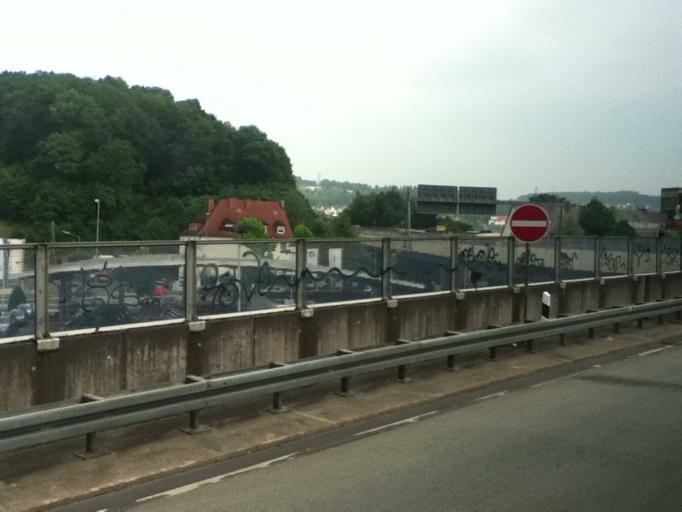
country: DE
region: North Rhine-Westphalia
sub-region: Regierungsbezirk Arnsberg
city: Siegen
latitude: 50.8996
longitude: 8.0251
